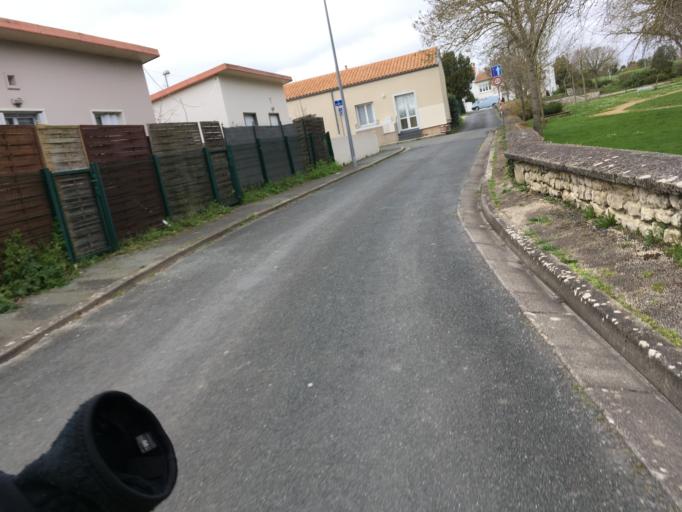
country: FR
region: Poitou-Charentes
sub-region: Departement de la Charente-Maritime
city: La Rochelle
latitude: 46.1780
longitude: -1.1452
